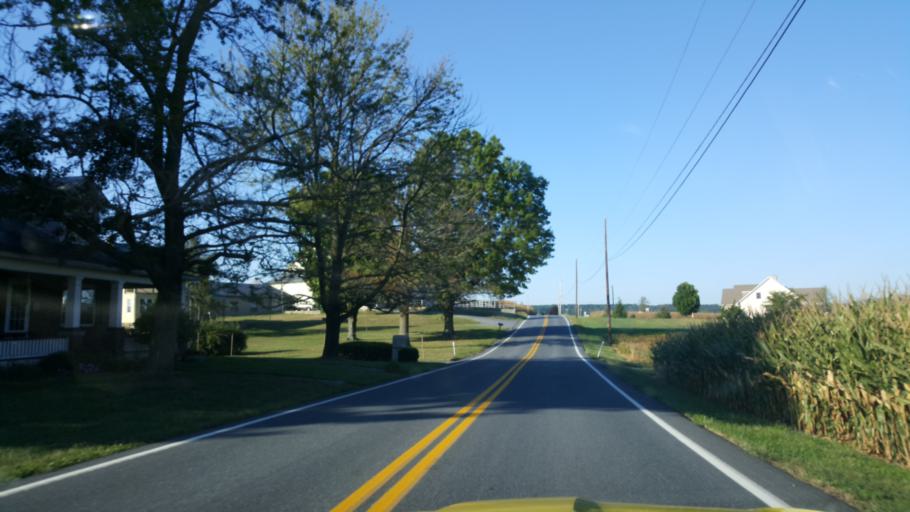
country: US
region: Pennsylvania
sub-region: Lancaster County
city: Rheems
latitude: 40.1998
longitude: -76.5162
